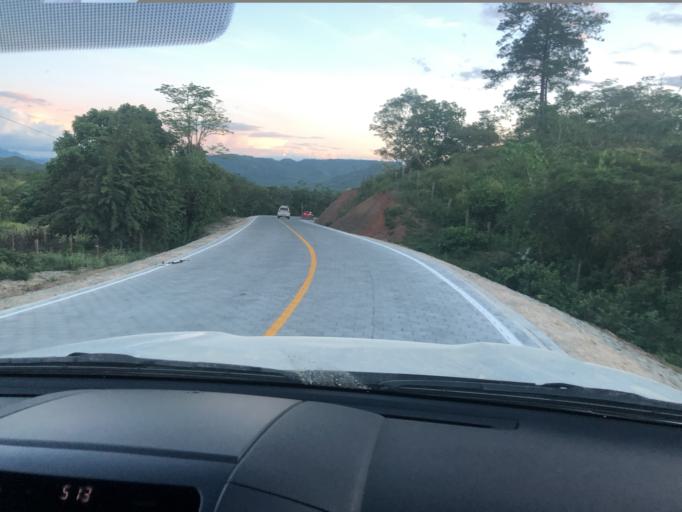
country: NI
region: Nueva Segovia
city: Ocotal
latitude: 13.6682
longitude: -86.6131
